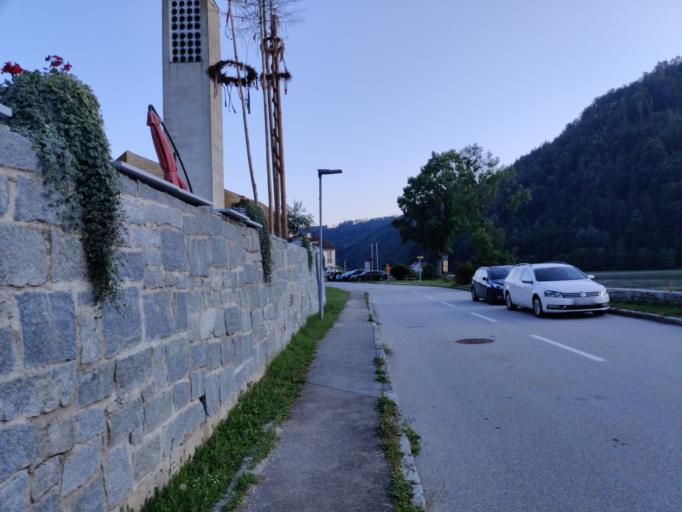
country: AT
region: Upper Austria
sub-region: Politischer Bezirk Rohrbach
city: Atzesberg
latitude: 48.4506
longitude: 13.9208
